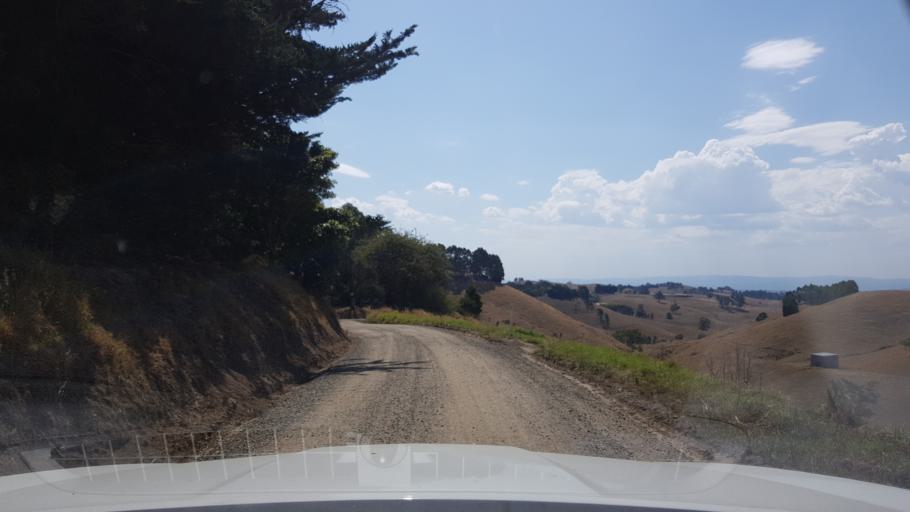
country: AU
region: Victoria
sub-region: Baw Baw
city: Warragul
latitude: -38.3001
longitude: 145.9085
